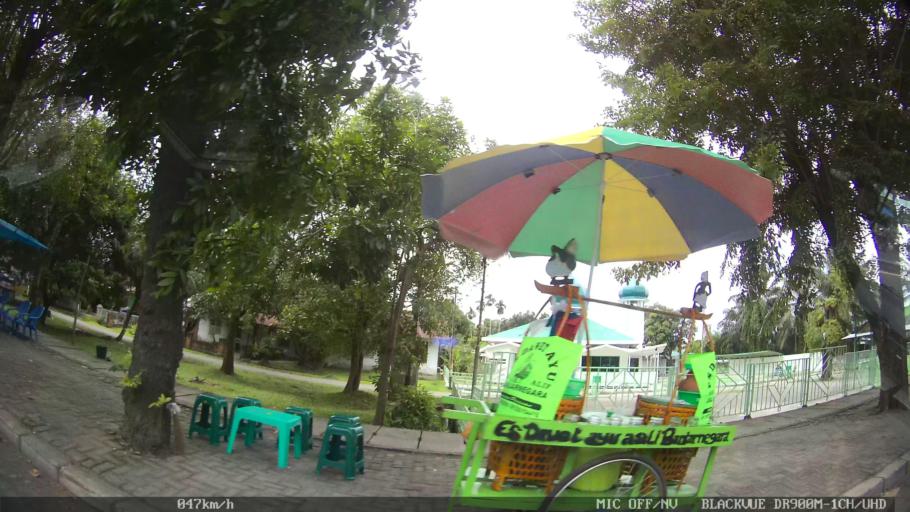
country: ID
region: North Sumatra
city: Sunggal
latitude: 3.5993
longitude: 98.5979
